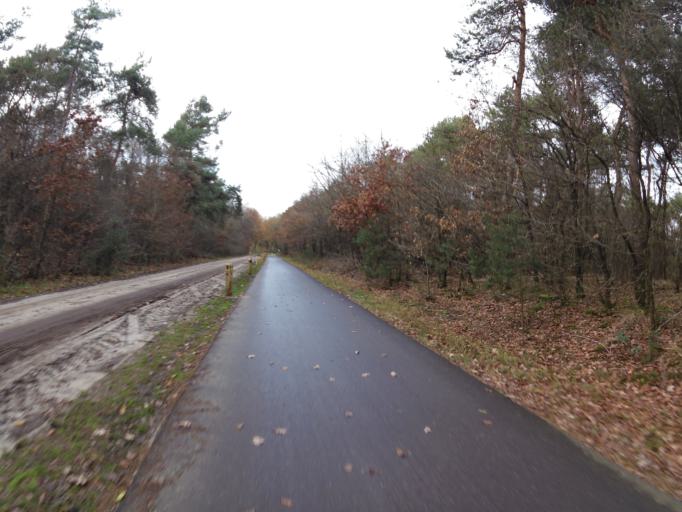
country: NL
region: North Brabant
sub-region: Gemeente Uden
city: Uden
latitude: 51.7067
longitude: 5.5929
